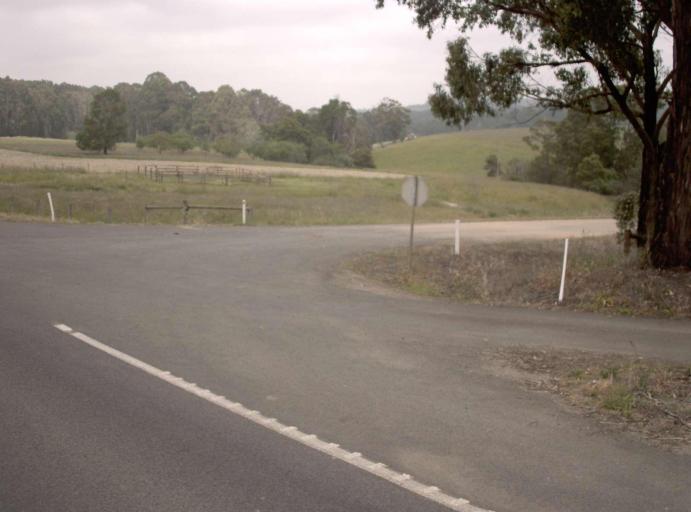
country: AU
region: Victoria
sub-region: Latrobe
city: Moe
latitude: -38.3554
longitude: 146.1902
